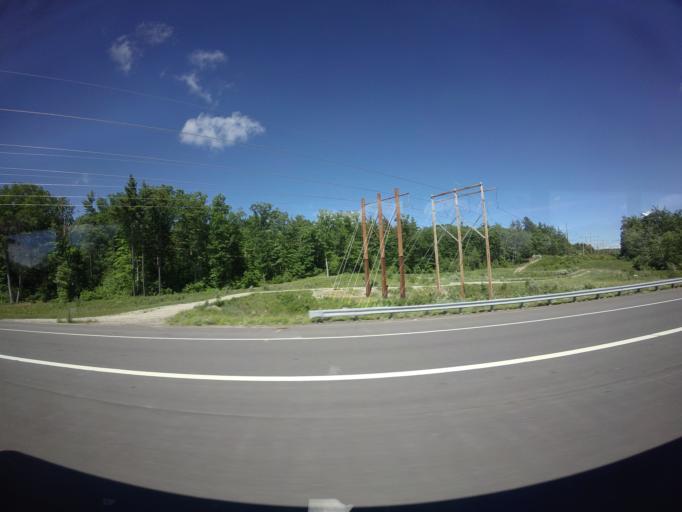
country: US
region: New Hampshire
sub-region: Rockingham County
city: Londonderry
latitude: 42.9220
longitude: -71.3750
